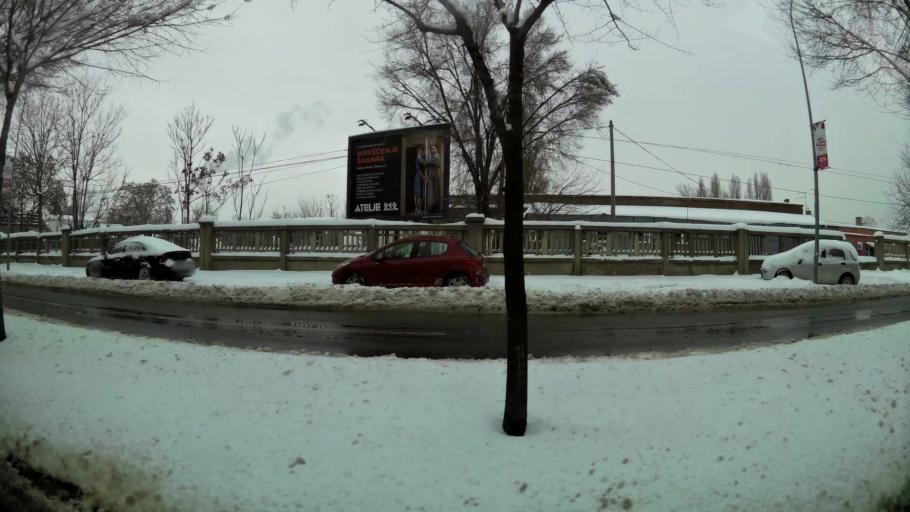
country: RS
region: Central Serbia
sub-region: Belgrade
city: Stari Grad
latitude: 44.8193
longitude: 20.4763
